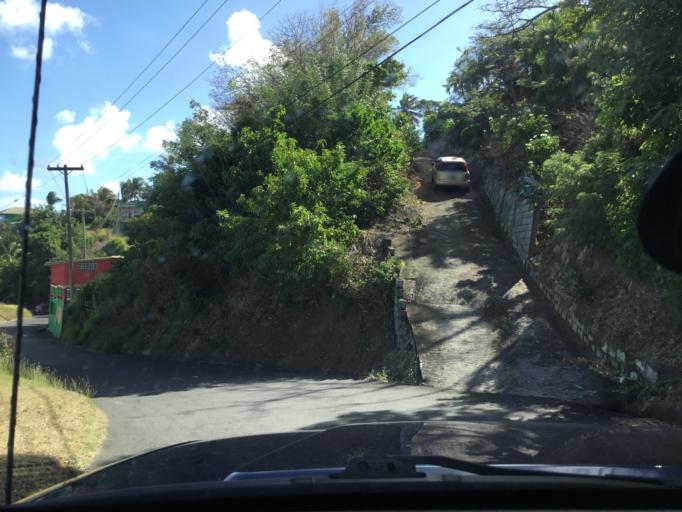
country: VC
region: Charlotte
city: Biabou
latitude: 13.1570
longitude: -61.1577
